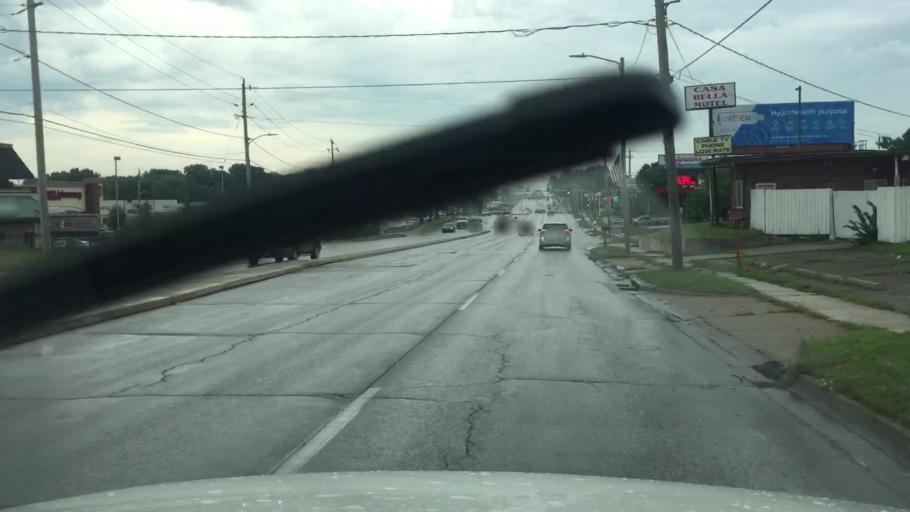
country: US
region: Iowa
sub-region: Polk County
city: Des Moines
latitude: 41.5566
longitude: -93.5970
